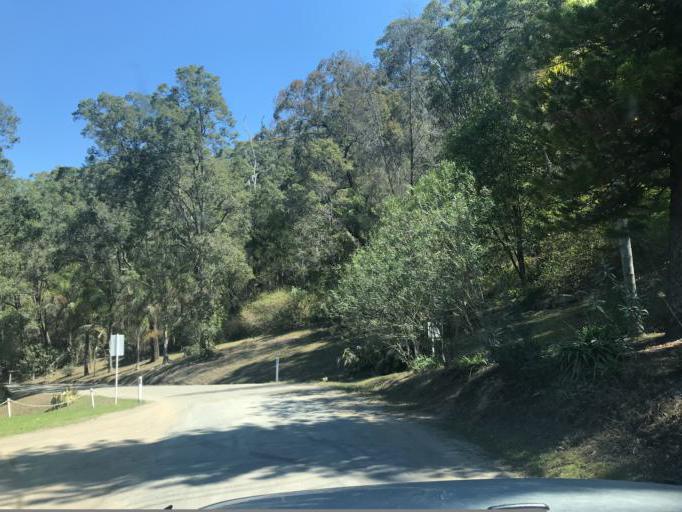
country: AU
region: New South Wales
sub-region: Hawkesbury
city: Pitt Town
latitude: -33.4225
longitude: 150.8951
